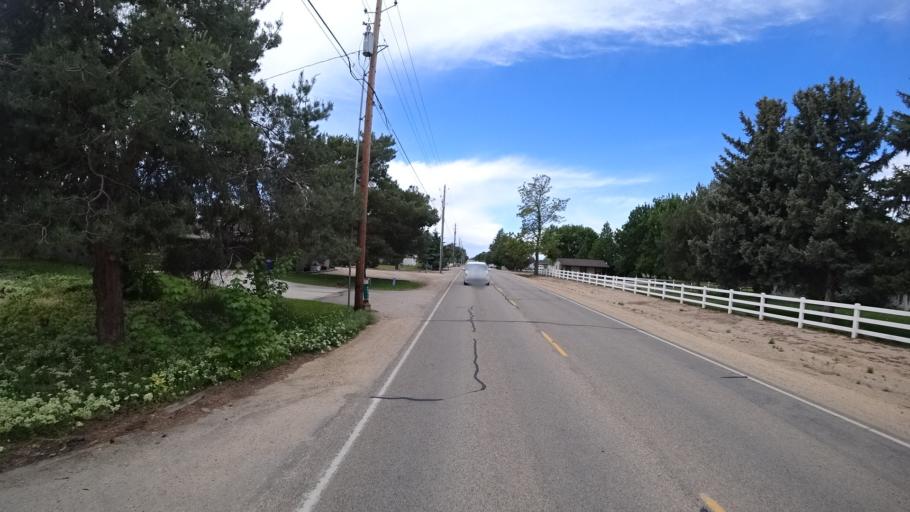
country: US
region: Idaho
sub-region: Ada County
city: Meridian
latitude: 43.5757
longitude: -116.3395
